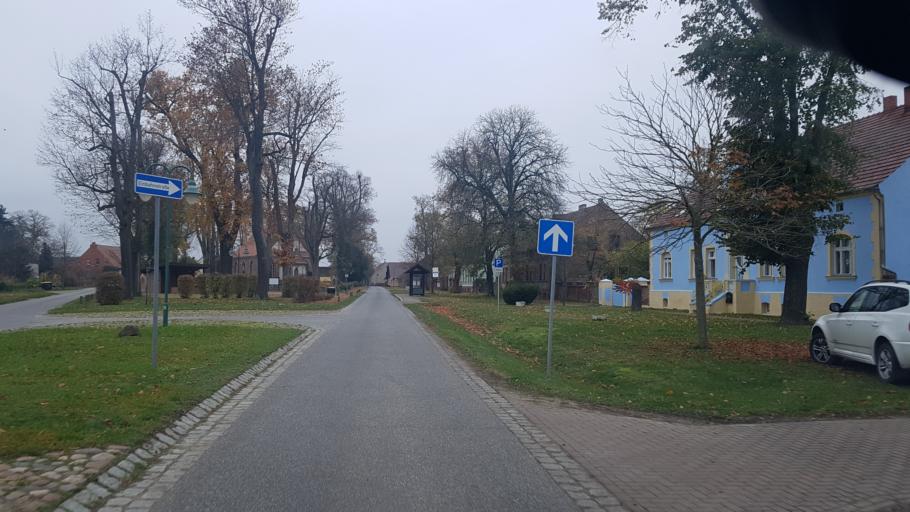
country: DE
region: Brandenburg
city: Schonermark
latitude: 52.9313
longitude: 13.1109
